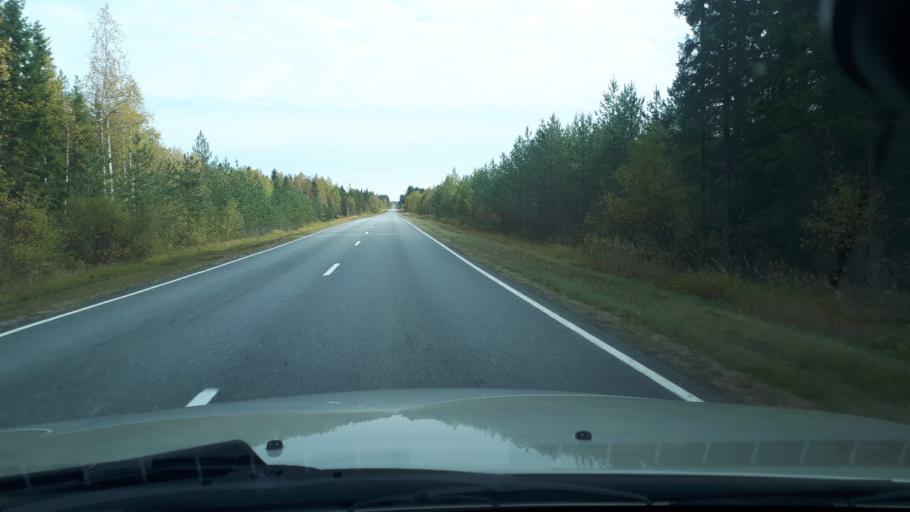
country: FI
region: Lapland
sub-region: Rovaniemi
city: Ranua
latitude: 65.9677
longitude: 26.0904
